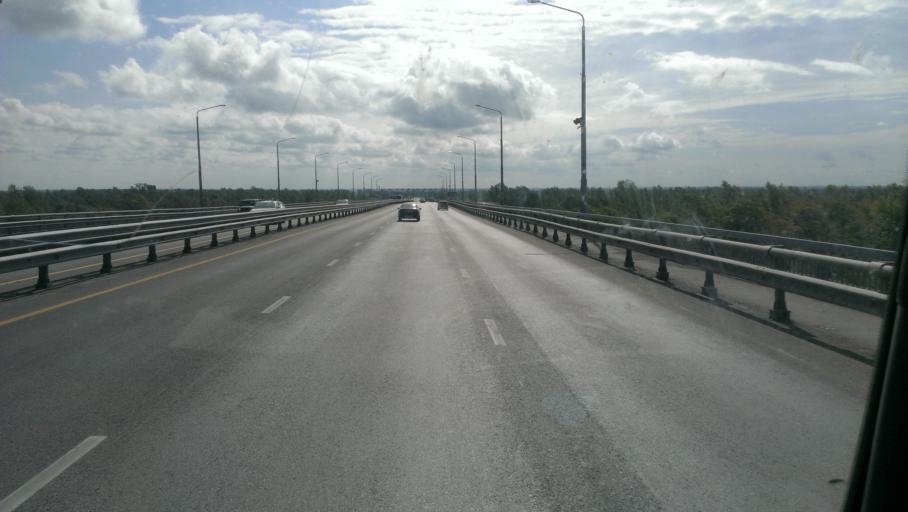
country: RU
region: Altai Krai
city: Zaton
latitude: 53.3224
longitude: 83.8065
